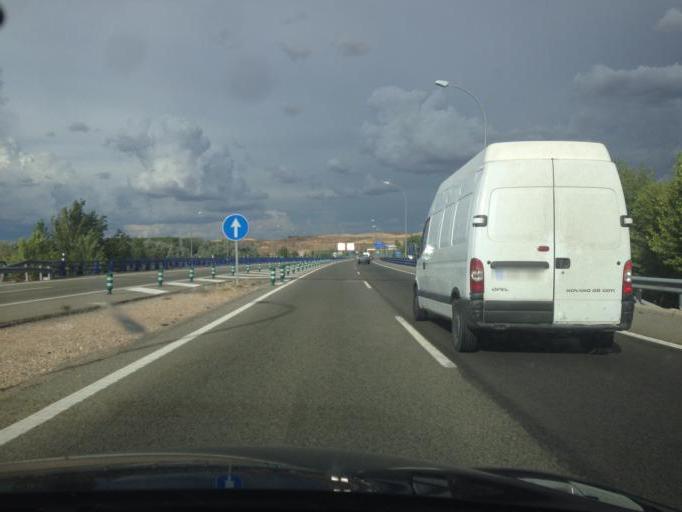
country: ES
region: Madrid
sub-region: Provincia de Madrid
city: Paracuellos de Jarama
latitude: 40.5432
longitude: -3.5597
